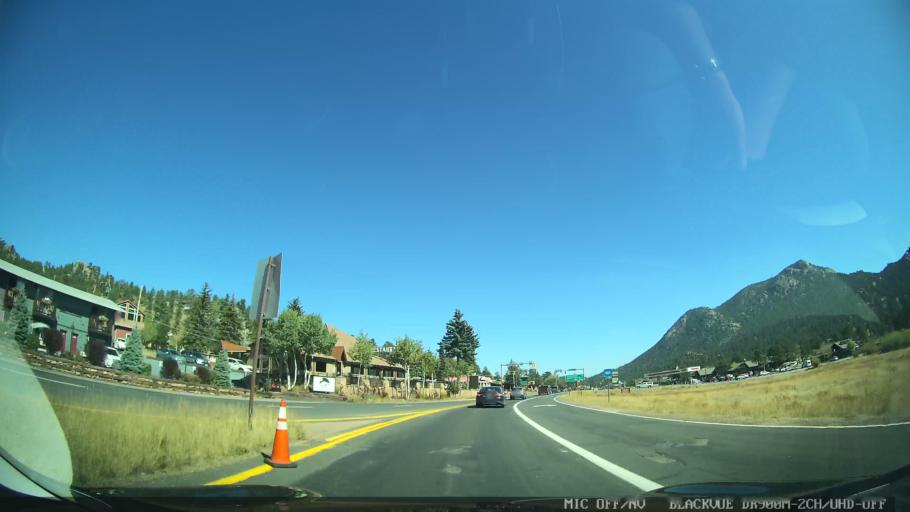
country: US
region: Colorado
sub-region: Larimer County
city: Estes Park
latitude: 40.3627
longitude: -105.5454
